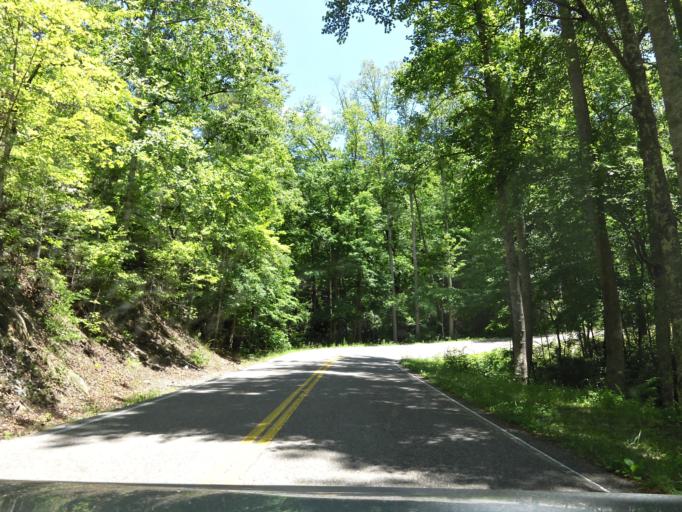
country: US
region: North Carolina
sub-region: Graham County
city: Robbinsville
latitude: 35.4779
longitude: -83.9261
